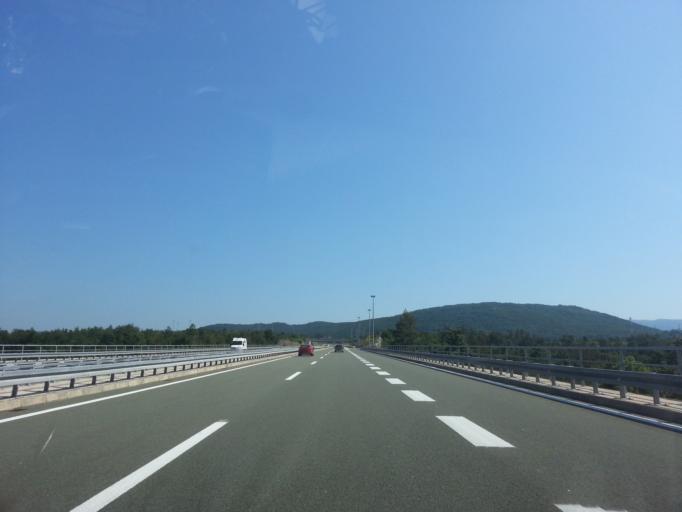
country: HR
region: Primorsko-Goranska
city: Klana
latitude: 45.4684
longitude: 14.2726
